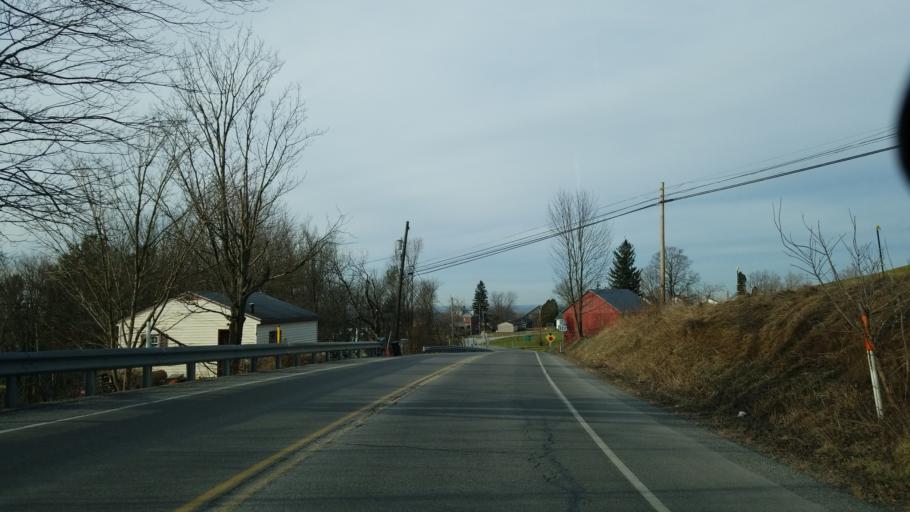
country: US
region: Pennsylvania
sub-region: Clearfield County
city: Sandy
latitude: 41.0520
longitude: -78.7151
